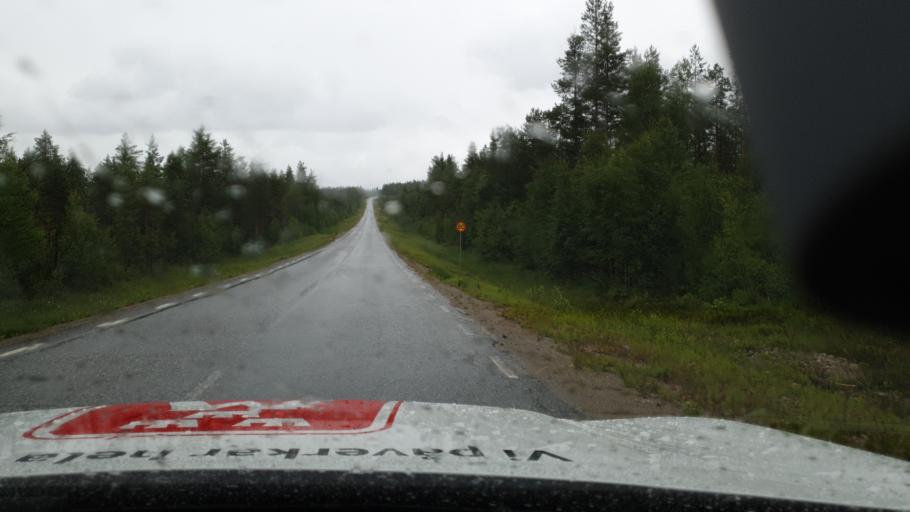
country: SE
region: Vaesterbotten
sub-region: Vindelns Kommun
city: Vindeln
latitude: 64.5125
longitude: 19.7935
